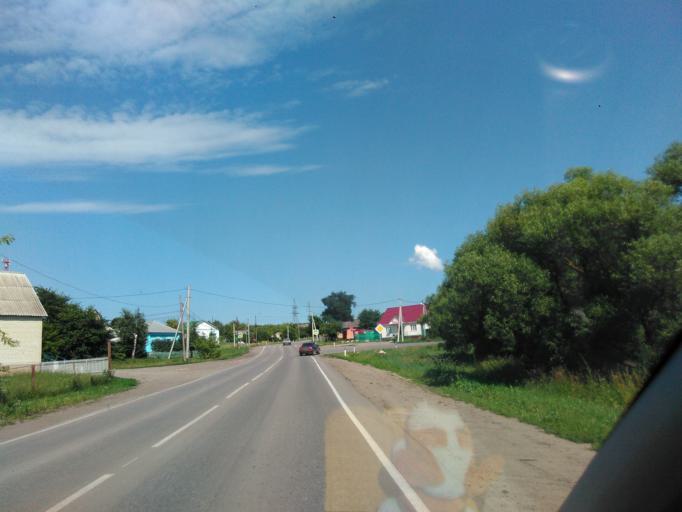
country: RU
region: Penza
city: Belinskiy
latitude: 52.9671
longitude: 43.4407
